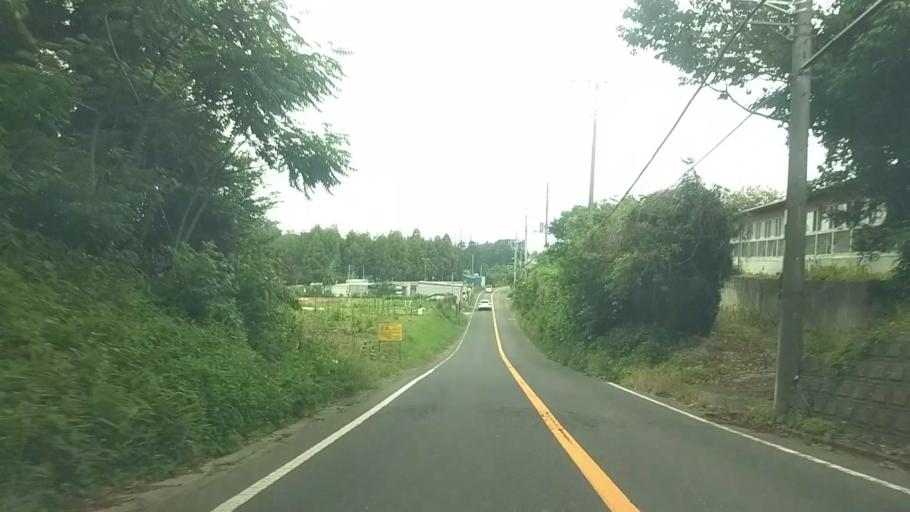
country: JP
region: Kanagawa
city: Fujisawa
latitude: 35.3543
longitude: 139.4352
